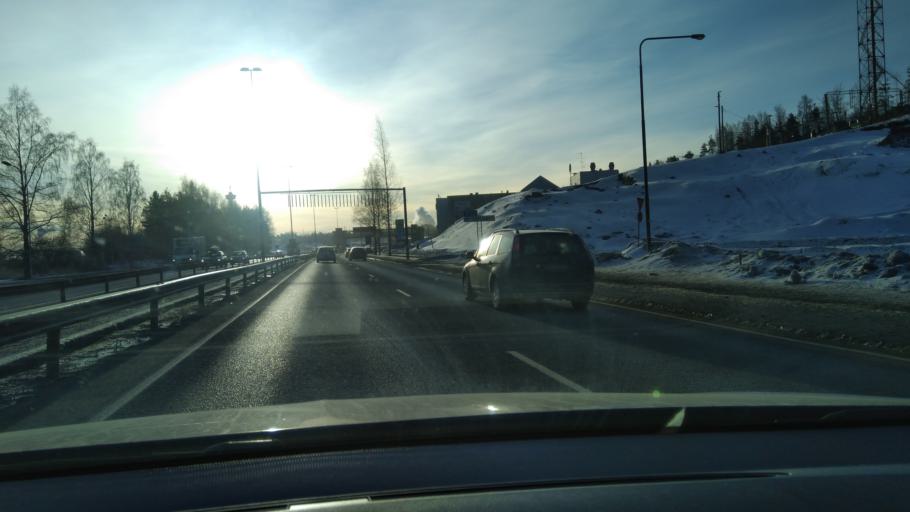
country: FI
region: Pirkanmaa
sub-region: Tampere
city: Tampere
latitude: 61.5071
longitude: 23.7088
